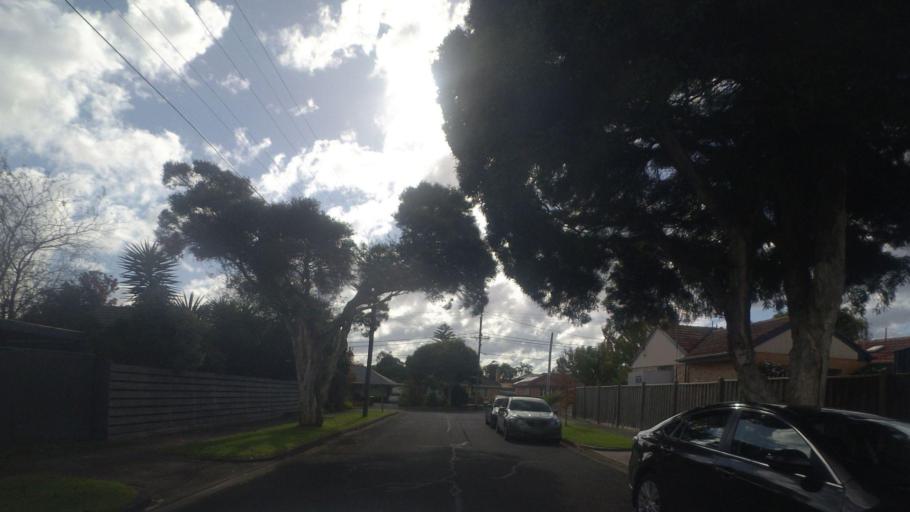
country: AU
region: Victoria
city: Forest Hill
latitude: -37.8424
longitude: 145.1781
